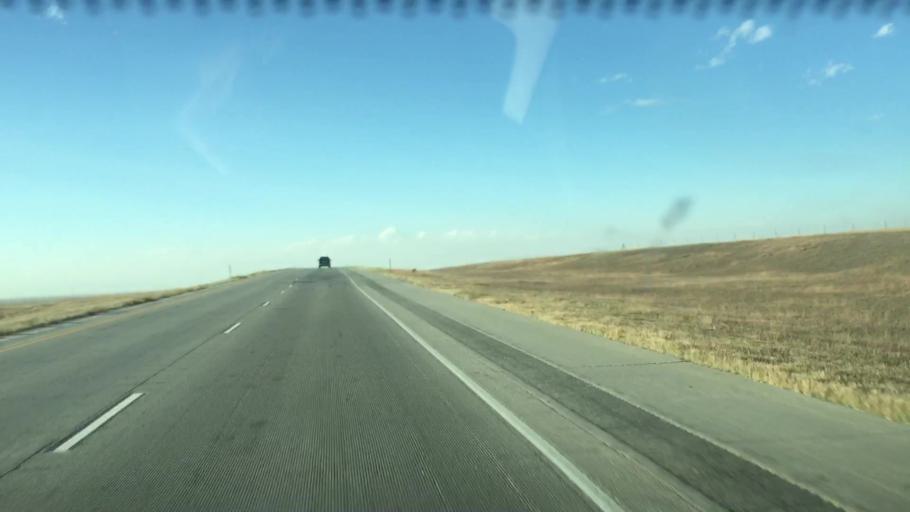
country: US
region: Colorado
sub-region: Lincoln County
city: Limon
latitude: 39.3992
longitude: -103.8926
